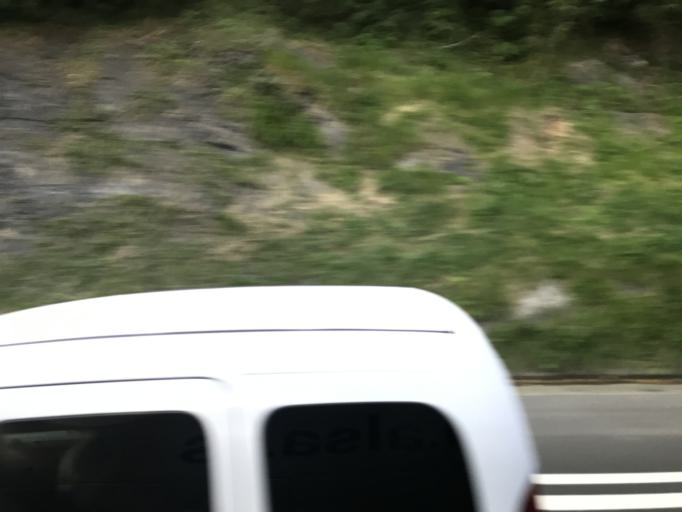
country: ES
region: Basque Country
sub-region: Provincia de Guipuzcoa
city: Beasain
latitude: 43.0455
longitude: -2.2106
